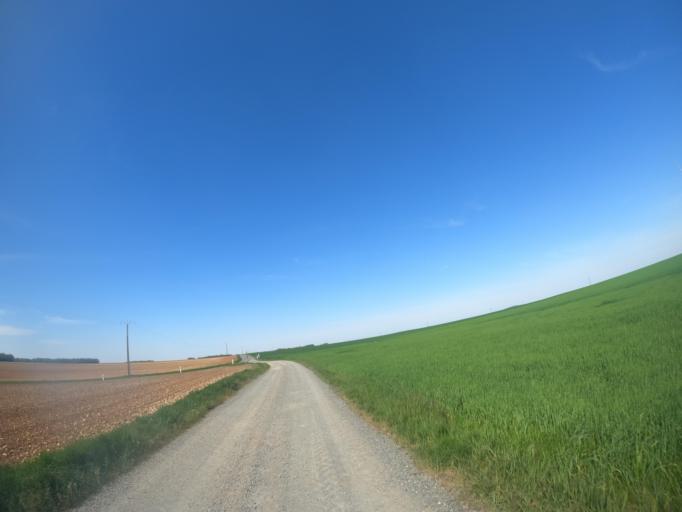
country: FR
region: Poitou-Charentes
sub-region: Departement des Deux-Sevres
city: Airvault
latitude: 46.8866
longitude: -0.1277
